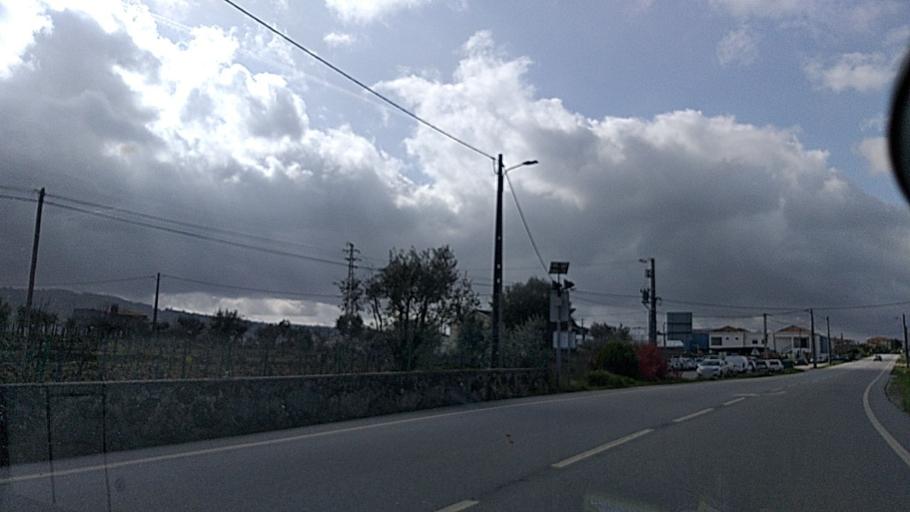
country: PT
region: Viseu
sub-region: Satao
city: Satao
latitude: 40.6669
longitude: -7.7125
